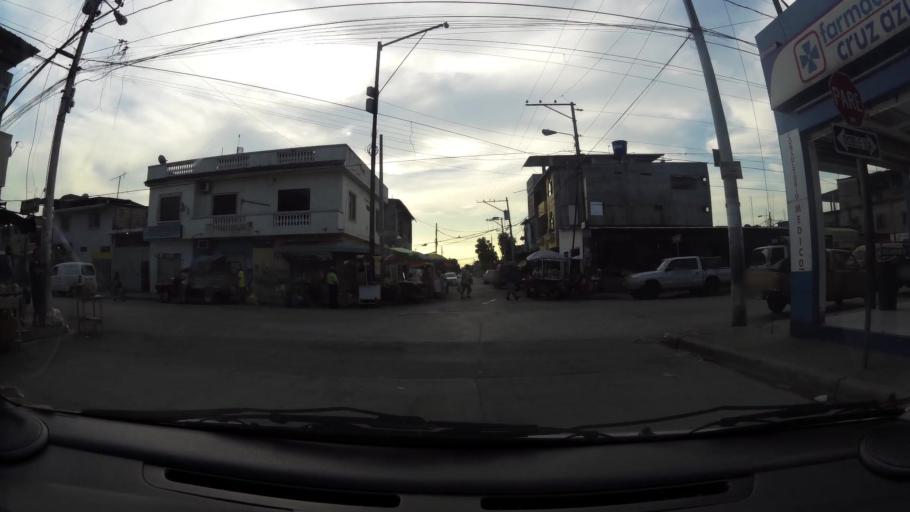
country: EC
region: Guayas
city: Eloy Alfaro
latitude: -2.0909
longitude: -79.9038
